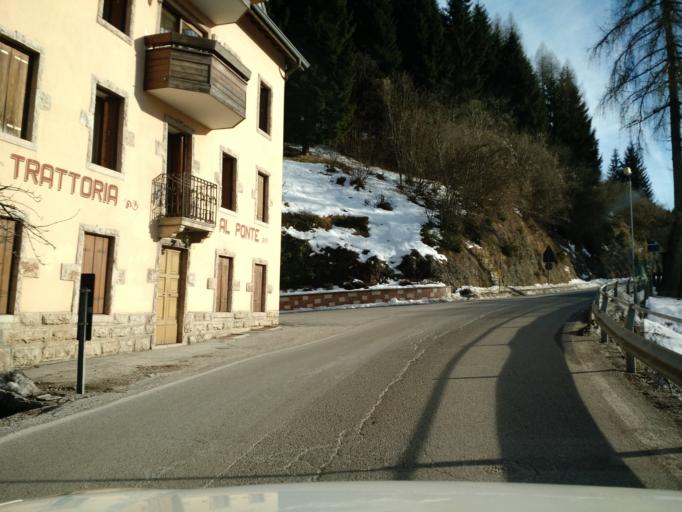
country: IT
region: Veneto
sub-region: Provincia di Vicenza
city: Canove di Roana
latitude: 45.8769
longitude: 11.4751
